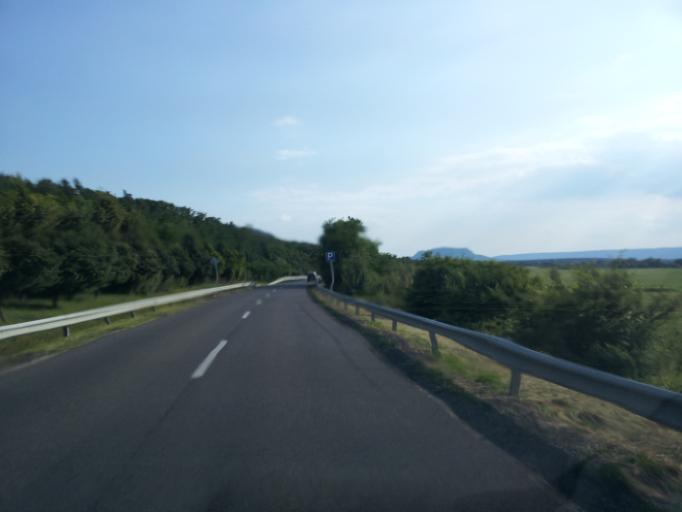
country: HU
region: Veszprem
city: Tapolca
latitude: 46.8974
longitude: 17.5203
